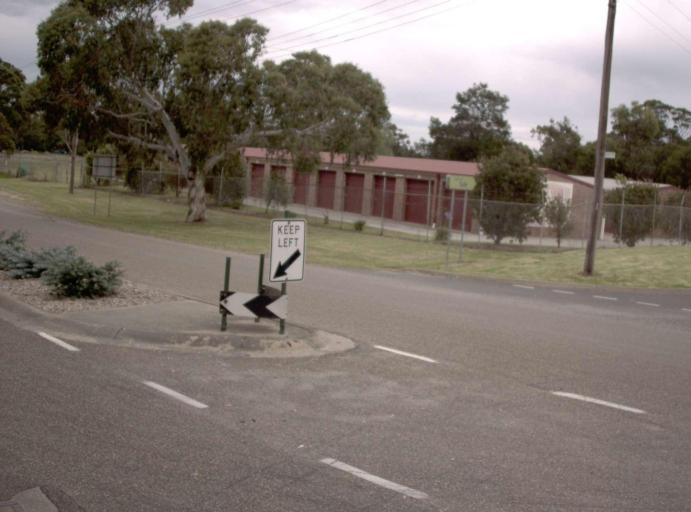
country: AU
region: Victoria
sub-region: Wellington
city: Sale
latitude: -38.1135
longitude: 147.0686
